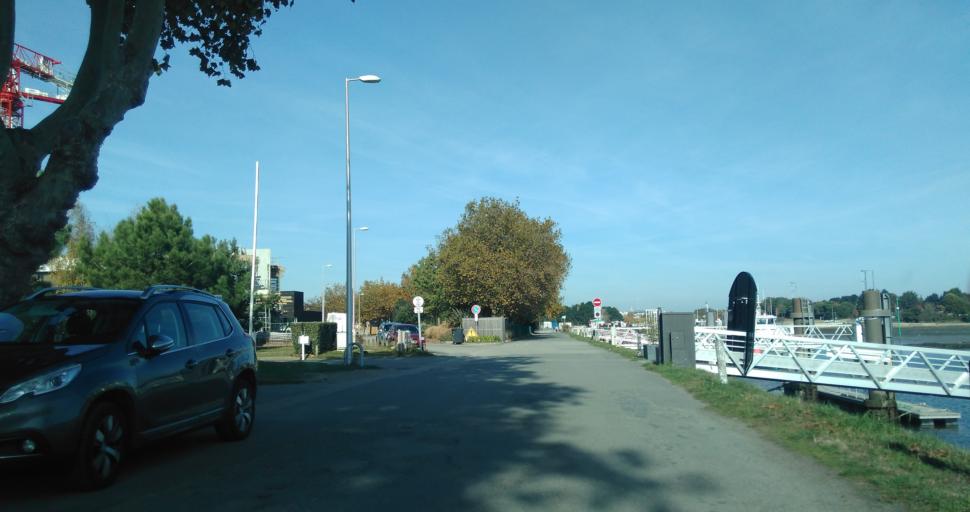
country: FR
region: Brittany
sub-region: Departement du Morbihan
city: Sene
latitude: 47.6358
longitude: -2.7623
